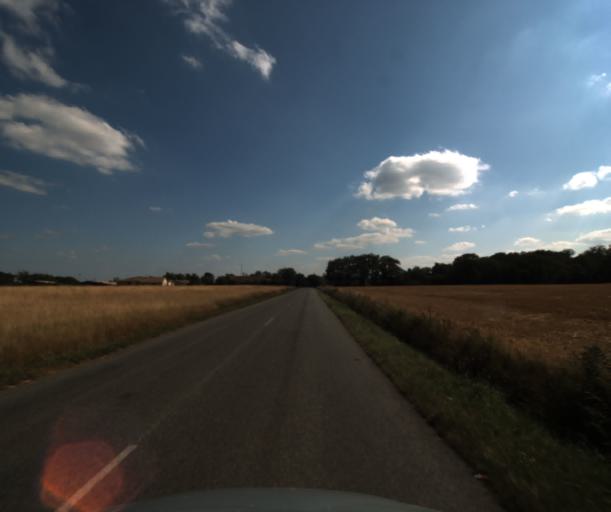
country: FR
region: Midi-Pyrenees
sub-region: Departement de la Haute-Garonne
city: Saint-Lys
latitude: 43.5208
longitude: 1.1805
